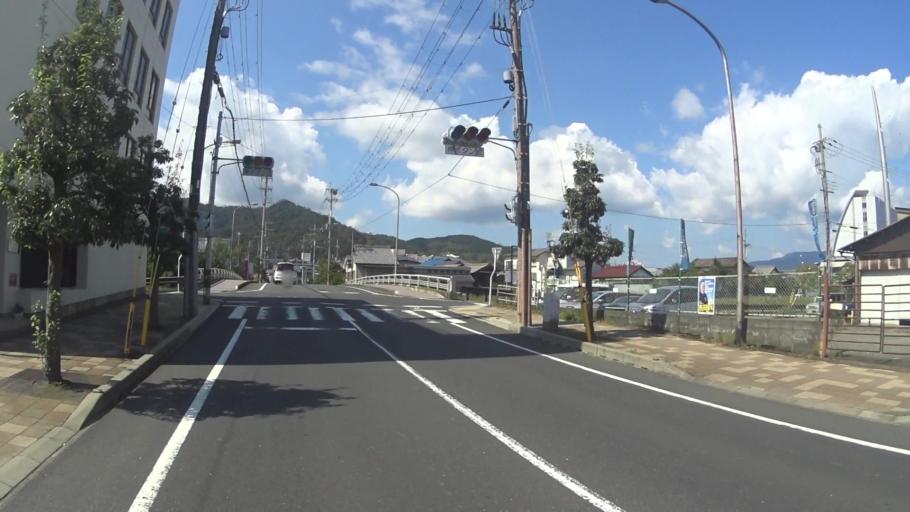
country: JP
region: Kyoto
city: Miyazu
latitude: 35.5370
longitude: 135.1974
